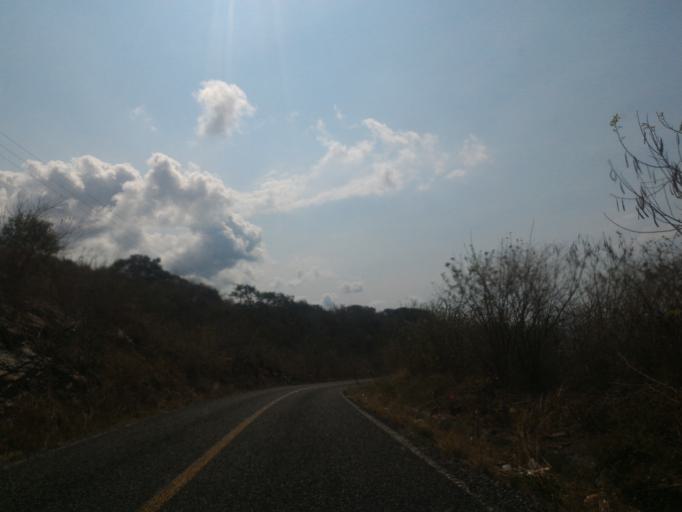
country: MX
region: Michoacan
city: Coahuayana Viejo
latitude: 18.4655
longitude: -103.5554
